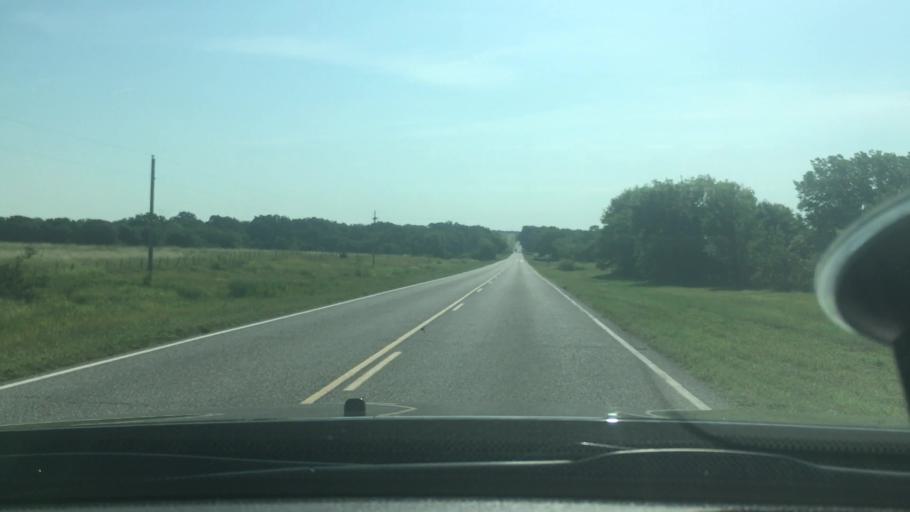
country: US
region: Oklahoma
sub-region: Garvin County
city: Pauls Valley
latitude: 34.6520
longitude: -97.3347
